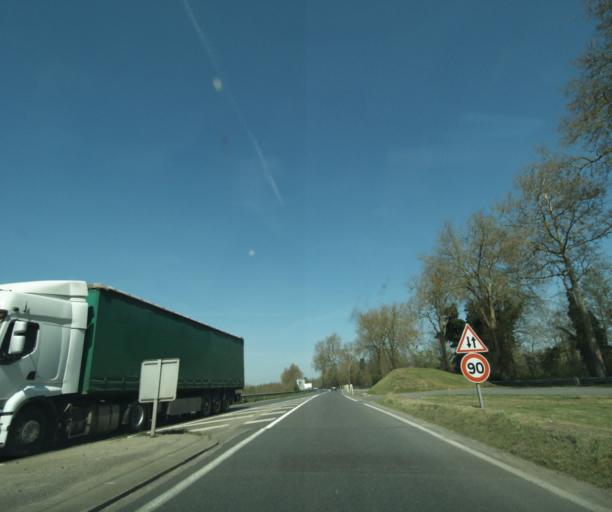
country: FR
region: Auvergne
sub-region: Departement de l'Allier
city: Trevol
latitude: 46.6254
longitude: 3.2859
